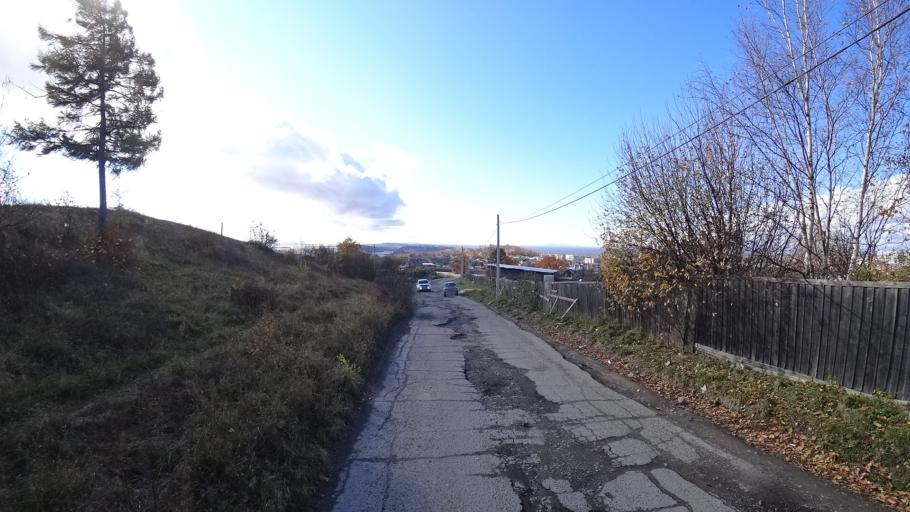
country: RU
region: Khabarovsk Krai
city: Amursk
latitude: 50.2368
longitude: 136.9240
